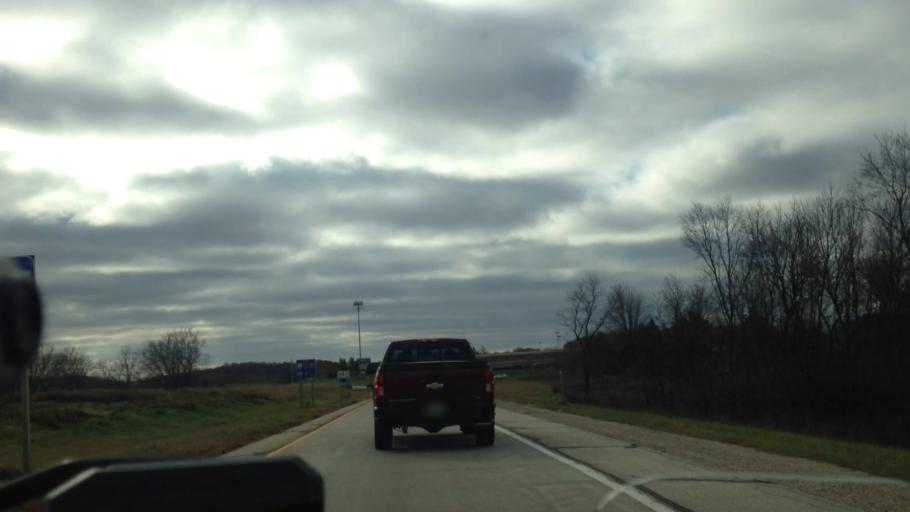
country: US
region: Wisconsin
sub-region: Washington County
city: West Bend
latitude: 43.4004
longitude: -88.1929
